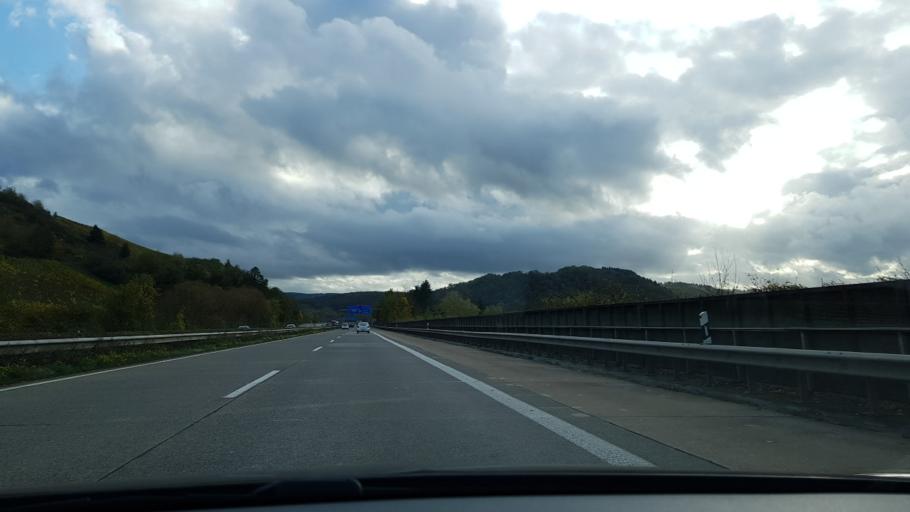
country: DE
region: Rheinland-Pfalz
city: Schweich
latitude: 49.8231
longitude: 6.7591
